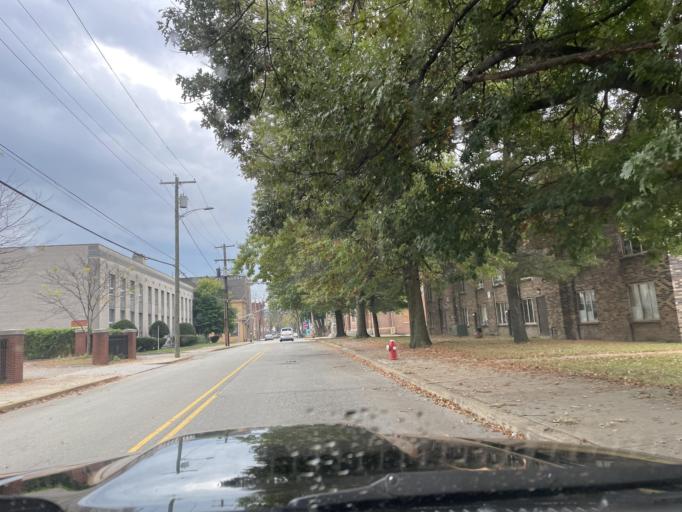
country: US
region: Pennsylvania
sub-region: Westmoreland County
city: New Kensington
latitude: 40.5692
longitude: -79.7661
